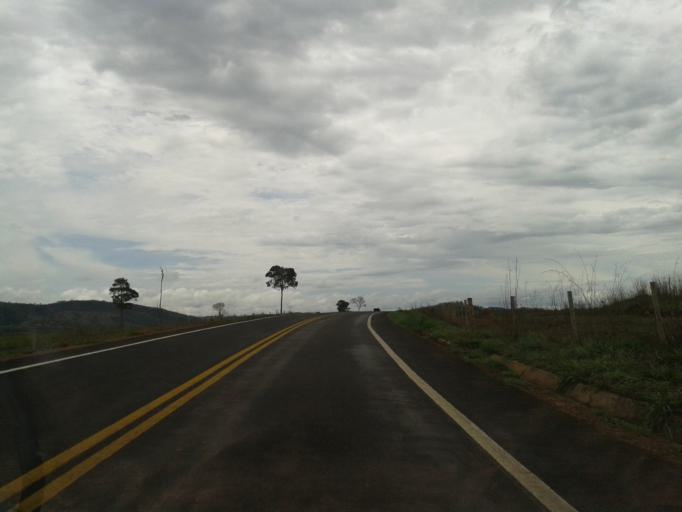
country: BR
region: Goias
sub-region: Buriti Alegre
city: Buriti Alegre
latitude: -18.1466
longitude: -48.8658
